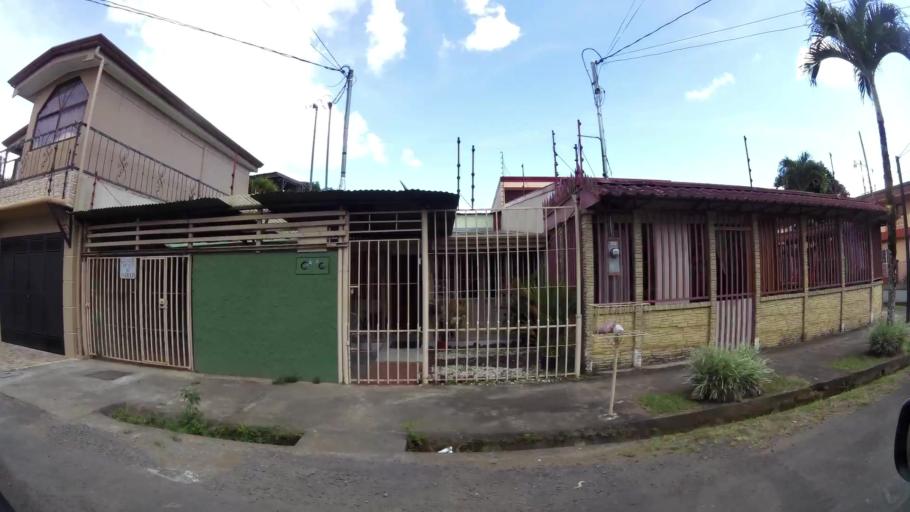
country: CR
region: San Jose
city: San Isidro
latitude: 9.3654
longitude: -83.7046
